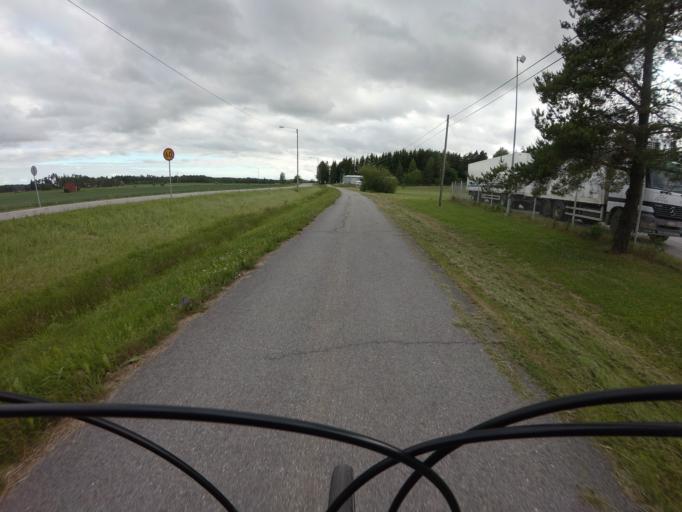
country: FI
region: Varsinais-Suomi
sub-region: Turku
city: Kaarina
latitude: 60.5008
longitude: 22.3654
